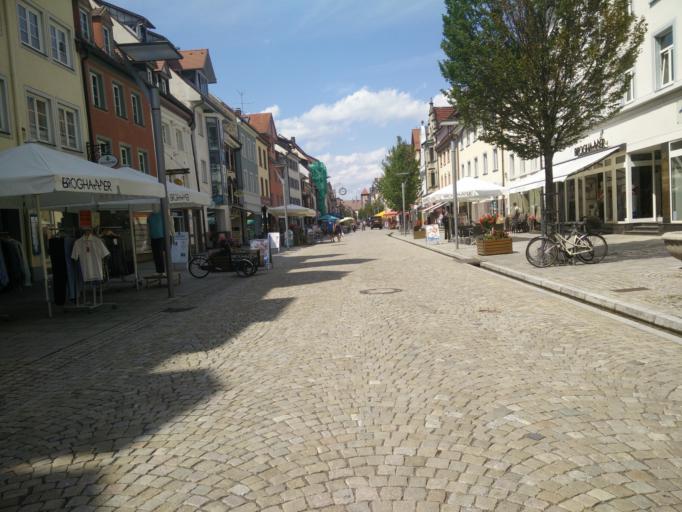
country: DE
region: Baden-Wuerttemberg
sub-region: Freiburg Region
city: Villingen-Schwenningen
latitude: 48.0569
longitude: 8.4610
